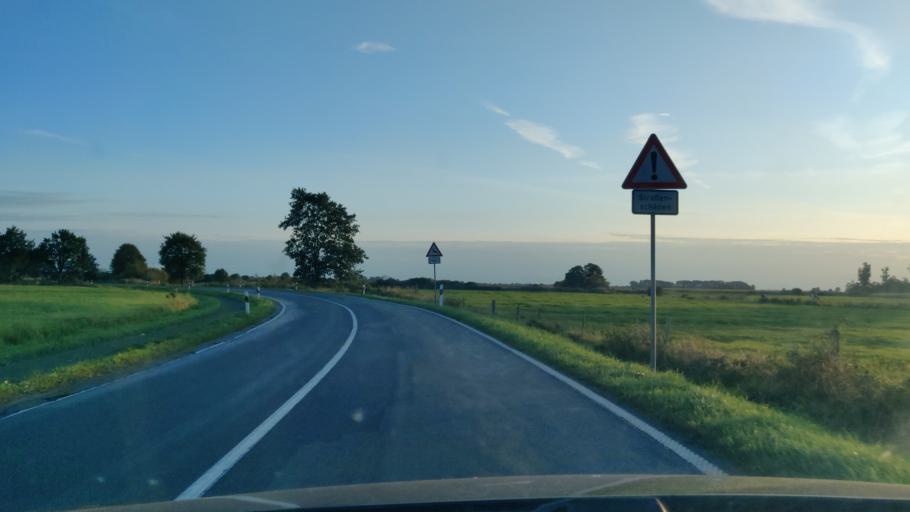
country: DE
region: Lower Saxony
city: Aurich
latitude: 53.4368
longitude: 7.3904
